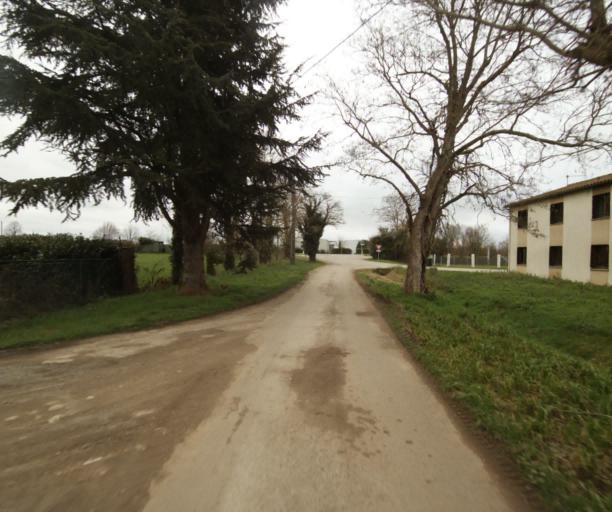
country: FR
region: Midi-Pyrenees
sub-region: Departement de l'Ariege
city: Pamiers
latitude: 43.1516
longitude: 1.6015
